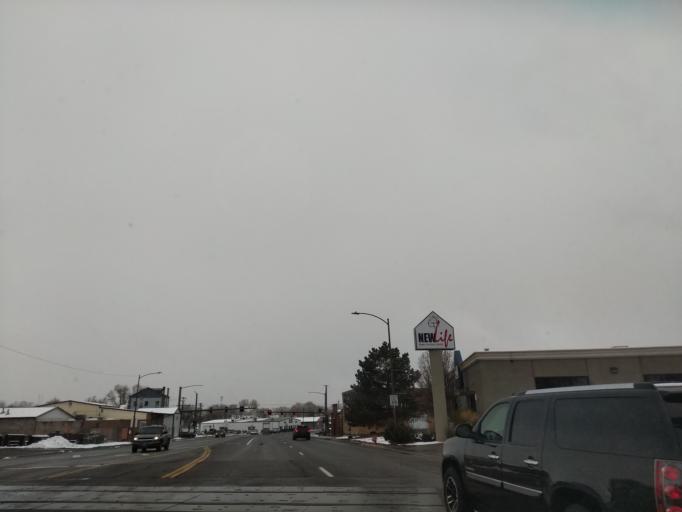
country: US
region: Colorado
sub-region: Montrose County
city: Montrose
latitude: 38.4775
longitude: -107.8797
